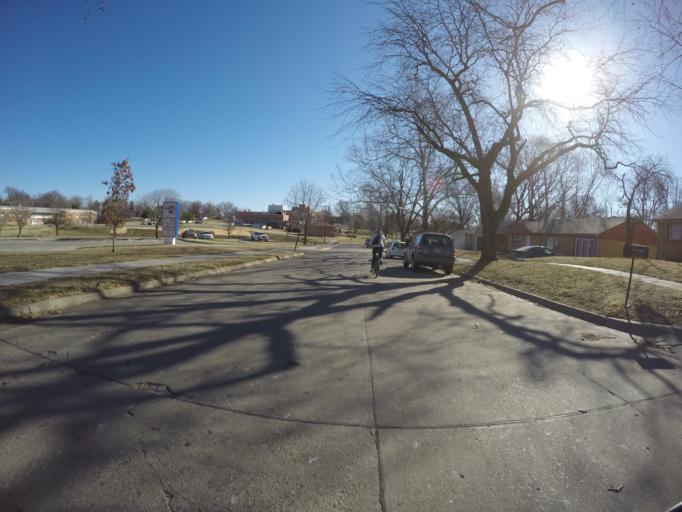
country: US
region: Kansas
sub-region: Riley County
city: Manhattan
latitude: 39.1912
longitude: -96.5928
